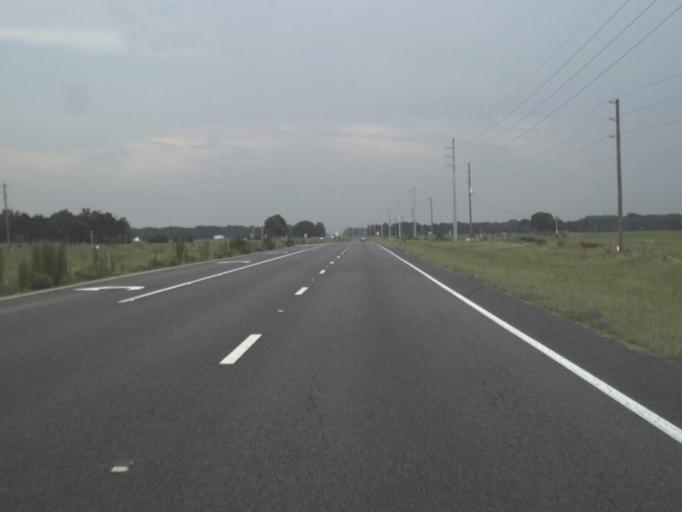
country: US
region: Florida
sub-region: Levy County
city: Chiefland
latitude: 29.4749
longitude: -82.7579
